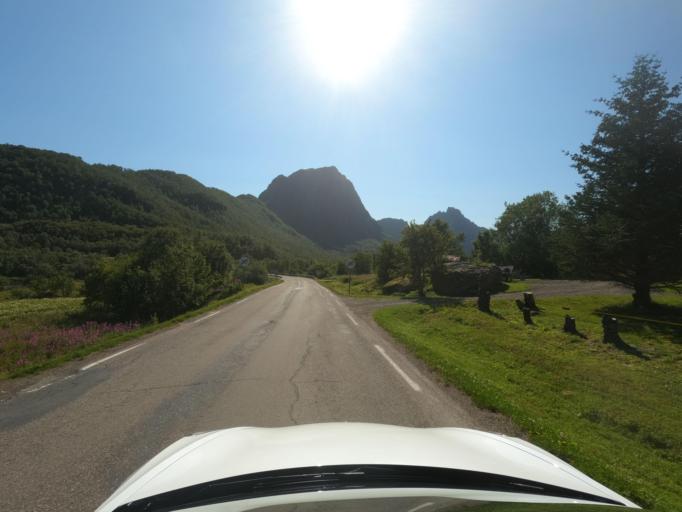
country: NO
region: Nordland
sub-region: Hadsel
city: Melbu
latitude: 68.4288
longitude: 14.8197
